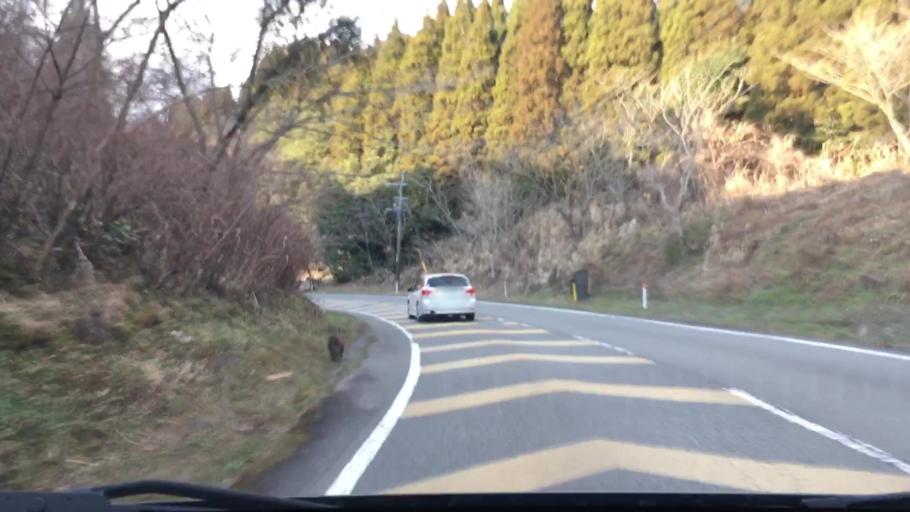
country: JP
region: Miyazaki
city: Miyazaki-shi
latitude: 31.7893
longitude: 131.3201
